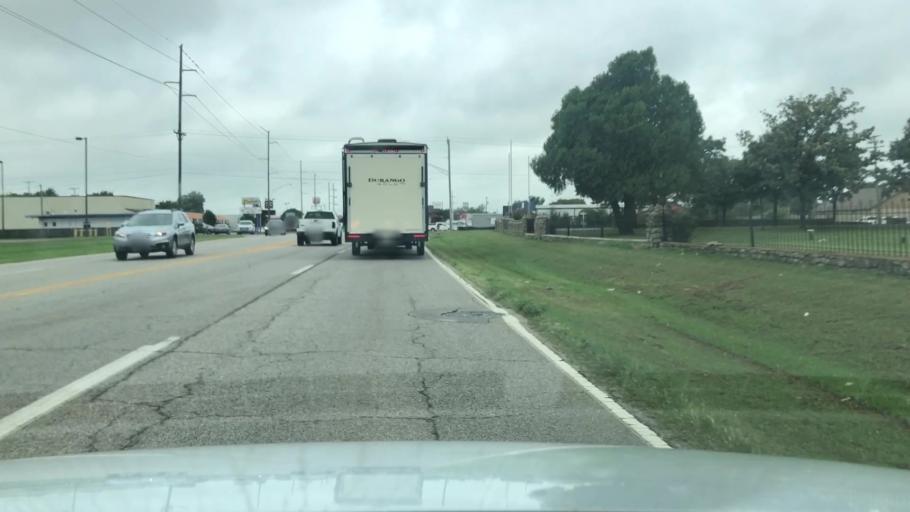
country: US
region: Oklahoma
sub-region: Washington County
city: Bartlesville
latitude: 36.7281
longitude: -95.9297
